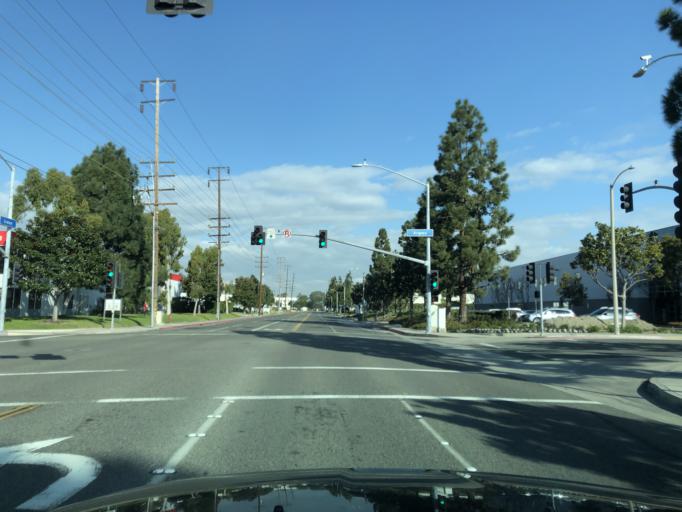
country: US
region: California
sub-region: Orange County
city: Westminster
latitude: 33.7408
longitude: -118.0328
